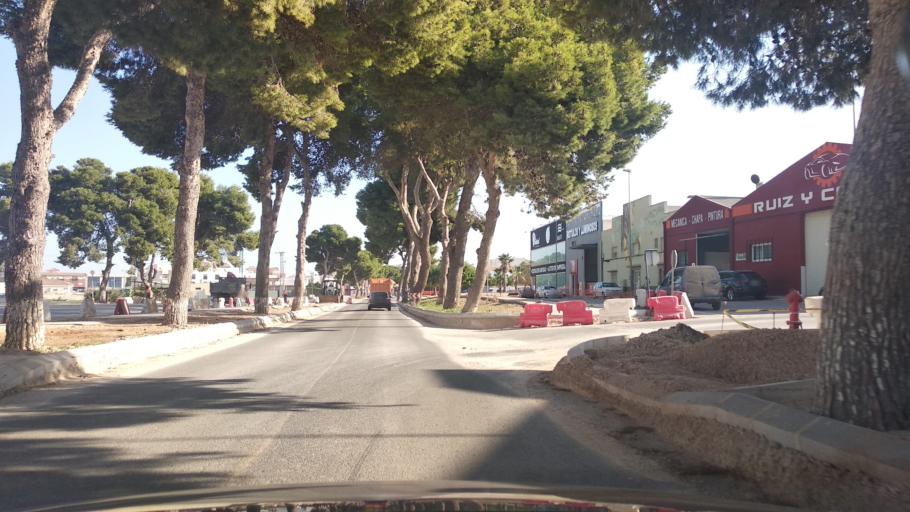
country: ES
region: Murcia
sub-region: Murcia
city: San Javier
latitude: 37.8105
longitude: -0.8381
